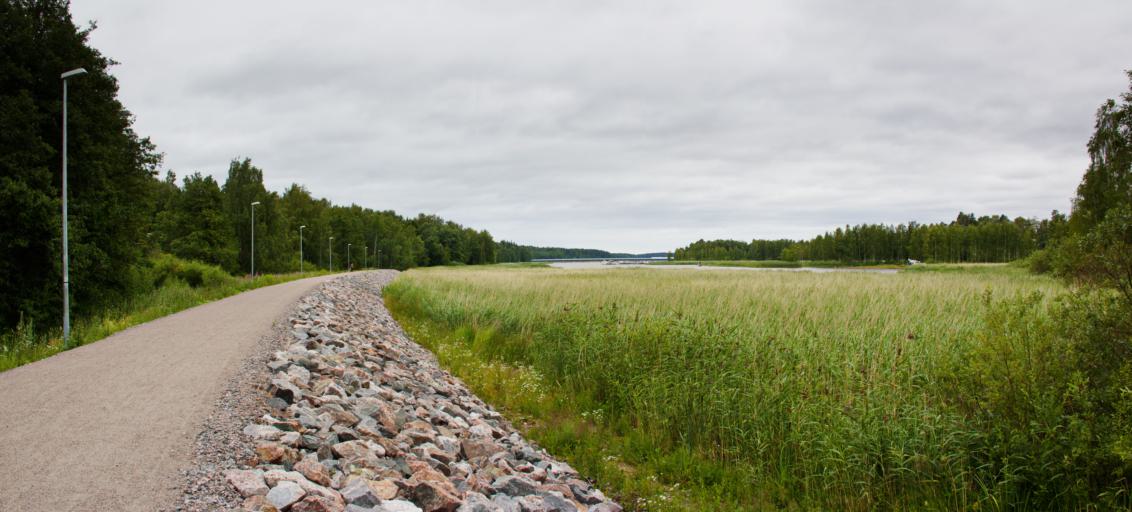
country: FI
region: Uusimaa
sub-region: Helsinki
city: Vantaa
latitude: 60.2199
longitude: 25.1249
